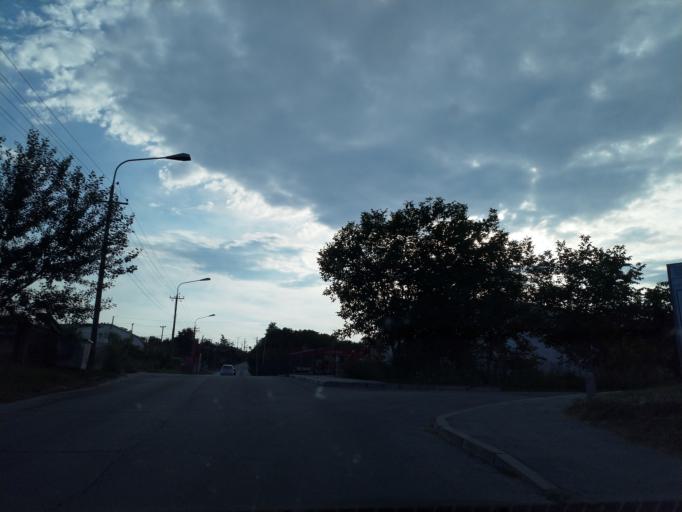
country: RS
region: Central Serbia
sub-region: Pomoravski Okrug
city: Jagodina
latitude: 43.9766
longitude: 21.2467
